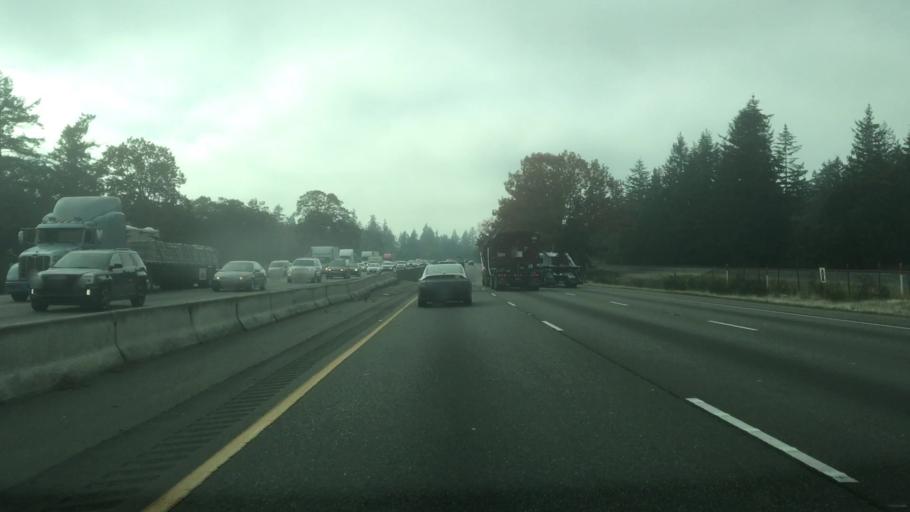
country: US
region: Washington
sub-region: Pierce County
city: Fort Lewis
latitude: 47.1139
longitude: -122.5652
